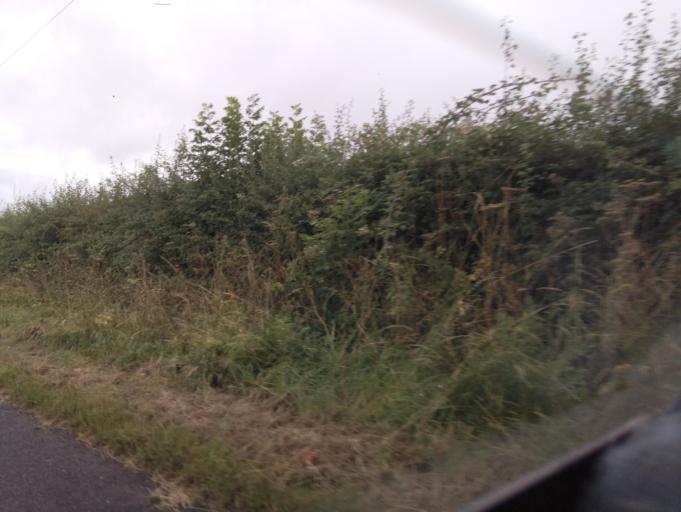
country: GB
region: England
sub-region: Worcestershire
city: Pershore
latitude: 52.1755
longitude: -2.1277
